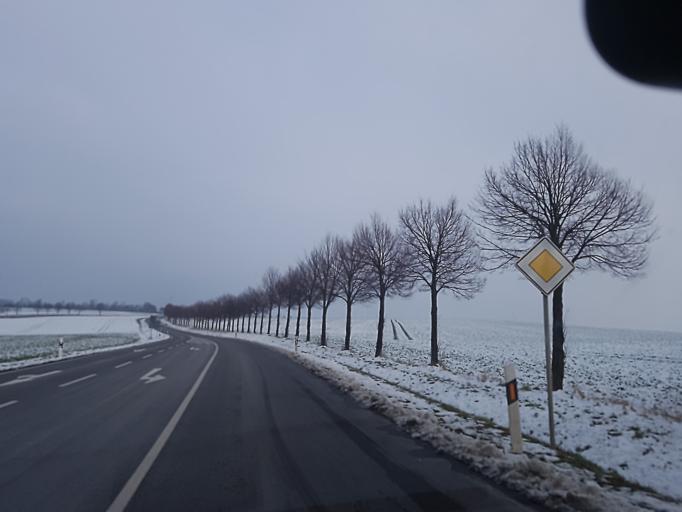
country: DE
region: Saxony
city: Bockelwitz
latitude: 51.1947
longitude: 12.9586
